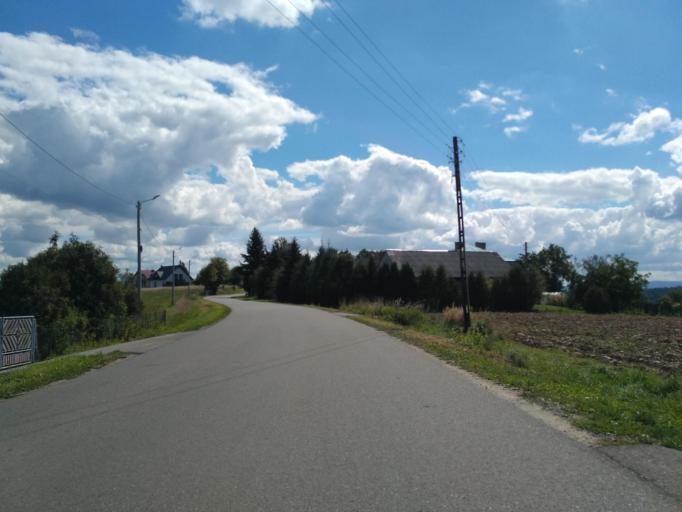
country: PL
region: Subcarpathian Voivodeship
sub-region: Powiat jasielski
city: Skolyszyn
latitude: 49.7746
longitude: 21.3682
